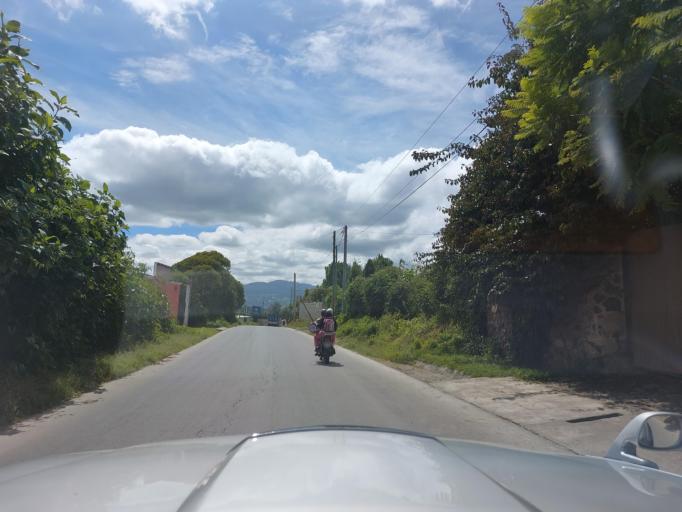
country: GT
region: Chimaltenango
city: San Andres Itzapa
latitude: 14.6182
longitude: -90.8324
